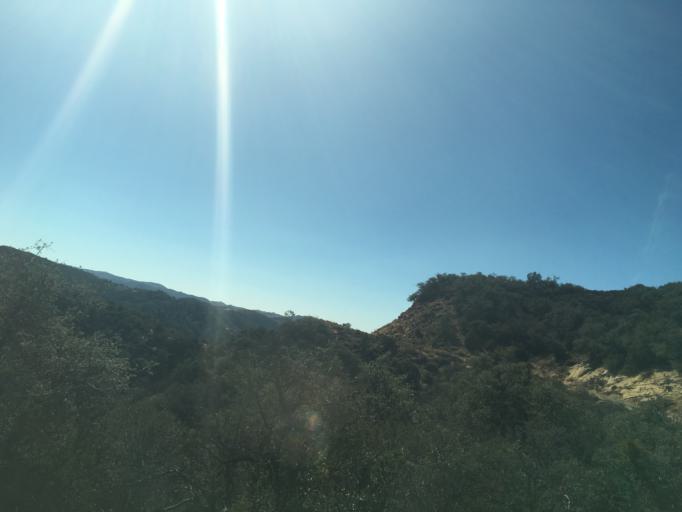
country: US
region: California
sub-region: Ventura County
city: Meiners Oaks
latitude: 34.6528
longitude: -119.3713
